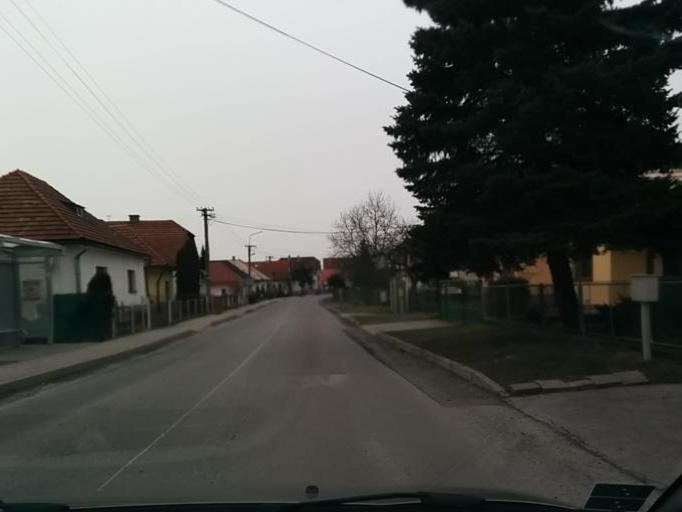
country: SK
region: Banskobystricky
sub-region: Okres Banska Bystrica
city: Zvolen
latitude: 48.6139
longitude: 19.1438
